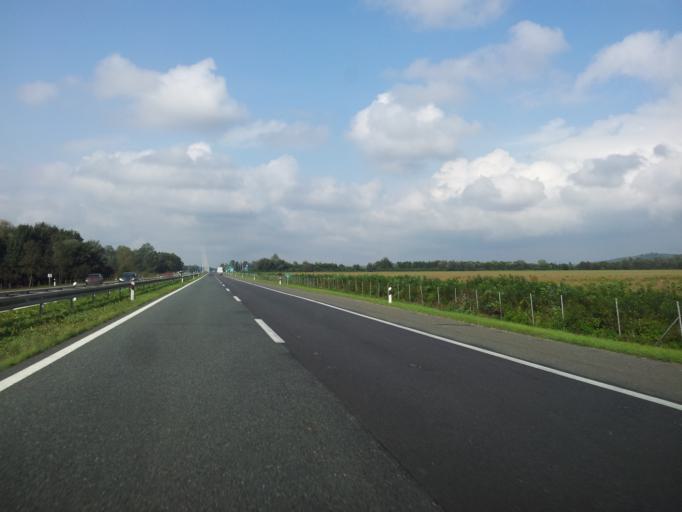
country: HR
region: Sisacko-Moslavacka
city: Novska
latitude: 45.3061
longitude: 17.0251
